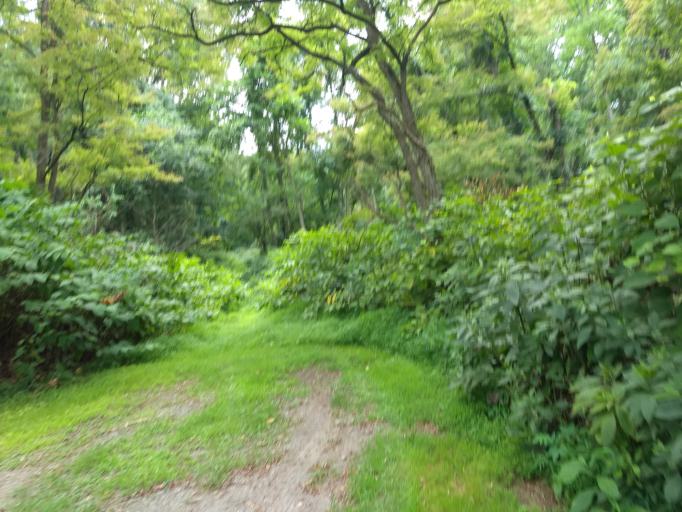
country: US
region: Pennsylvania
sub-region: Allegheny County
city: Brackenridge
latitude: 40.6098
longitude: -79.7157
